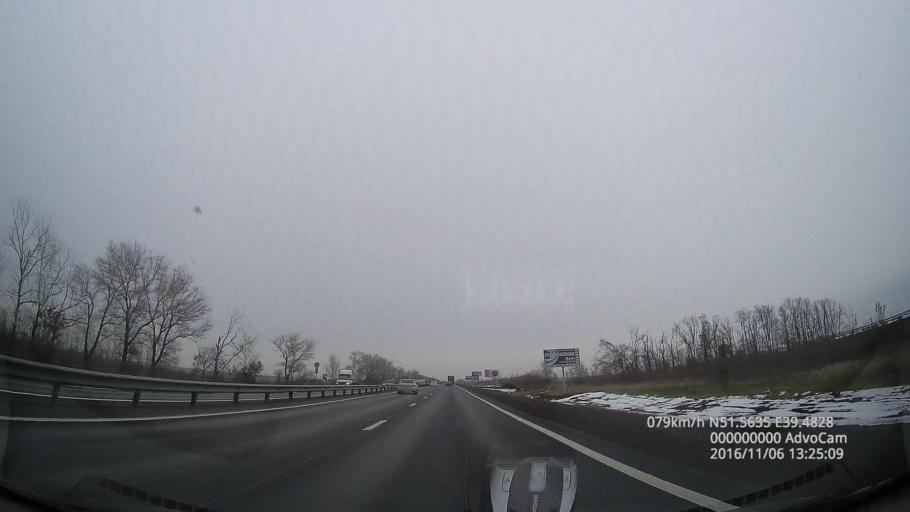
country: RU
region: Voronezj
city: Podkletnoye
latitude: 51.5601
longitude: 39.4861
